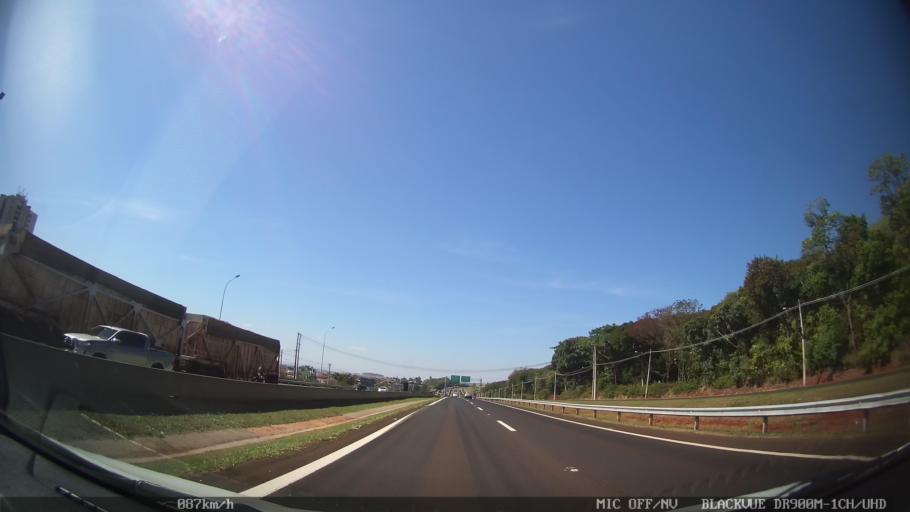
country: BR
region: Sao Paulo
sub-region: Ribeirao Preto
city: Ribeirao Preto
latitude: -21.2229
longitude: -47.7957
